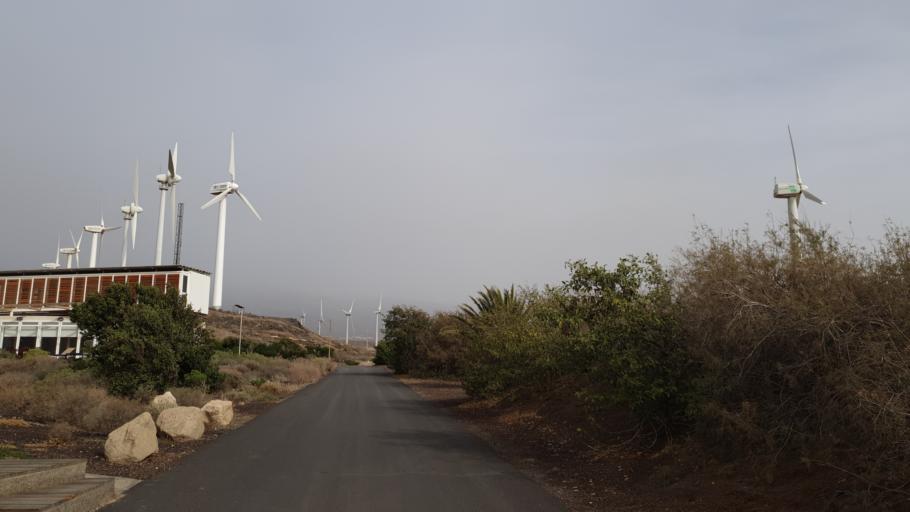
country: ES
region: Canary Islands
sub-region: Provincia de Santa Cruz de Tenerife
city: San Isidro
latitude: 28.0688
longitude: -16.5089
